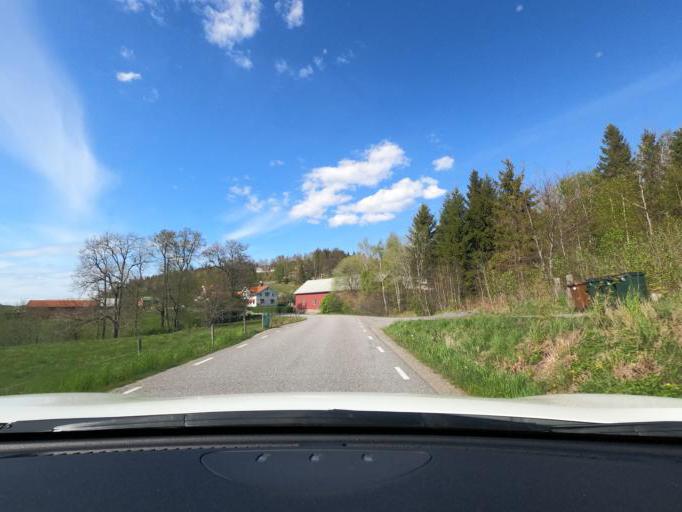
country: SE
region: Vaestra Goetaland
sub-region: Harryda Kommun
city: Ravlanda
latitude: 57.6340
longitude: 12.4988
